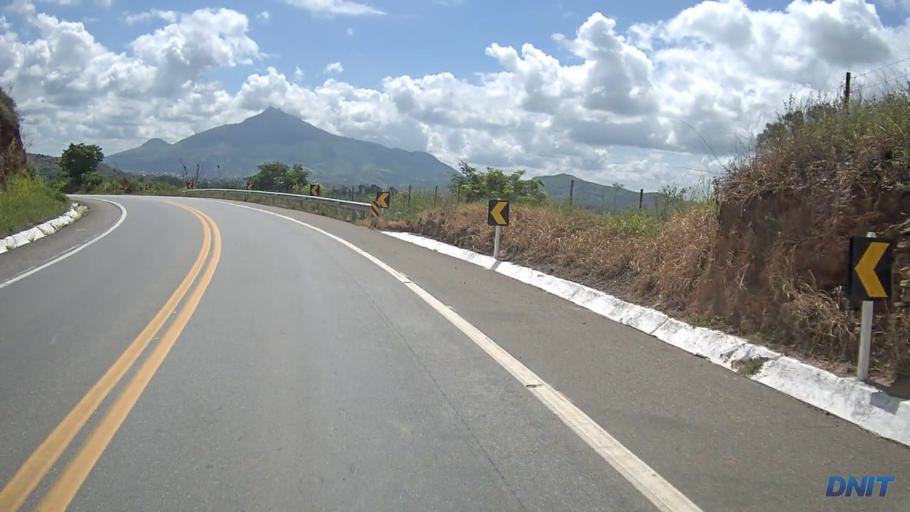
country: BR
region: Minas Gerais
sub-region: Governador Valadares
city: Governador Valadares
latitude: -18.9246
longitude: -42.0193
